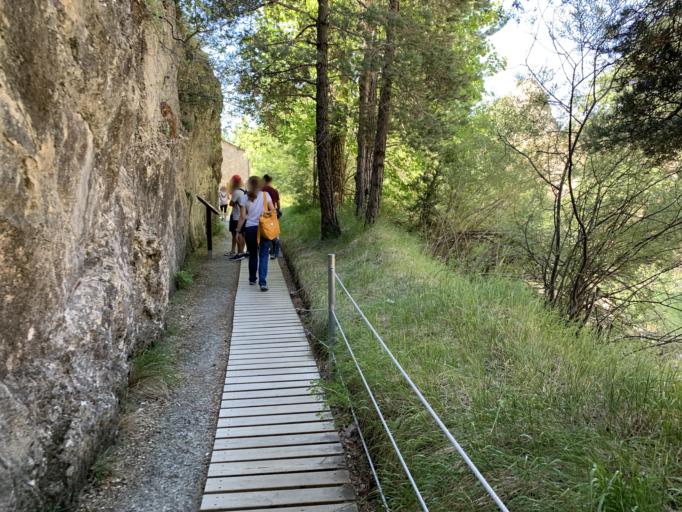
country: ES
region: Aragon
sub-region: Provincia de Huesca
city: Villanua
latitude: 42.6836
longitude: -0.5322
